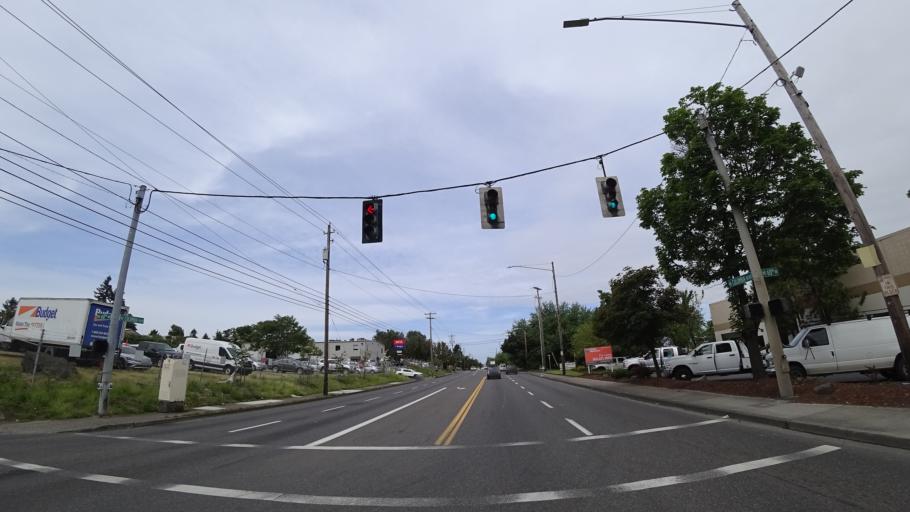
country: US
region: Oregon
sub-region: Multnomah County
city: Portland
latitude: 45.5688
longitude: -122.6006
